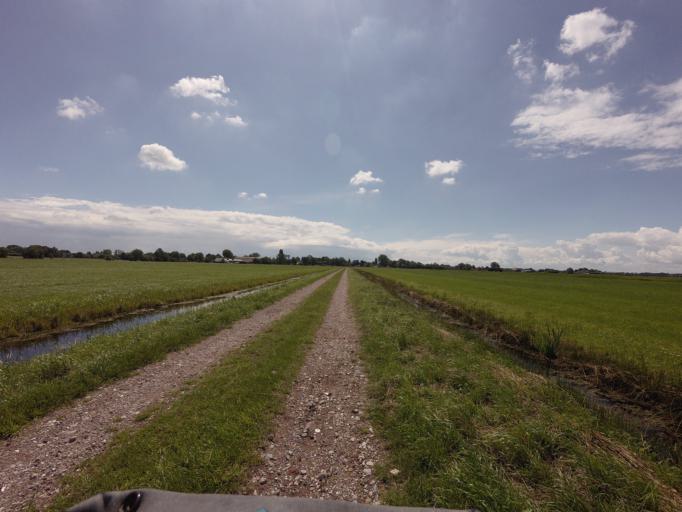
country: NL
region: South Holland
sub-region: Gemeente Schoonhoven
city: Schoonhoven
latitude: 51.9642
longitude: 4.8741
